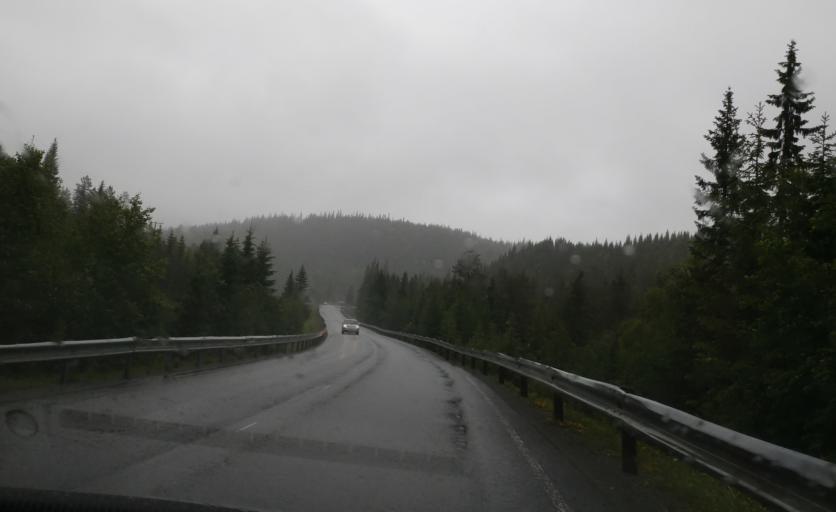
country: NO
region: Sor-Trondelag
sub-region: Selbu
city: Mebonden
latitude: 63.3384
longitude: 11.0833
